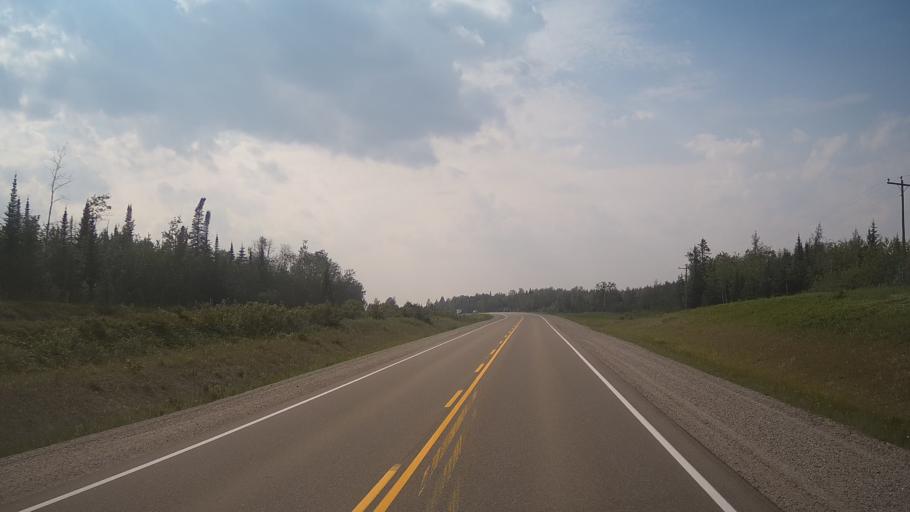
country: CA
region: Ontario
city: Kapuskasing
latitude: 49.5032
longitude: -82.7466
